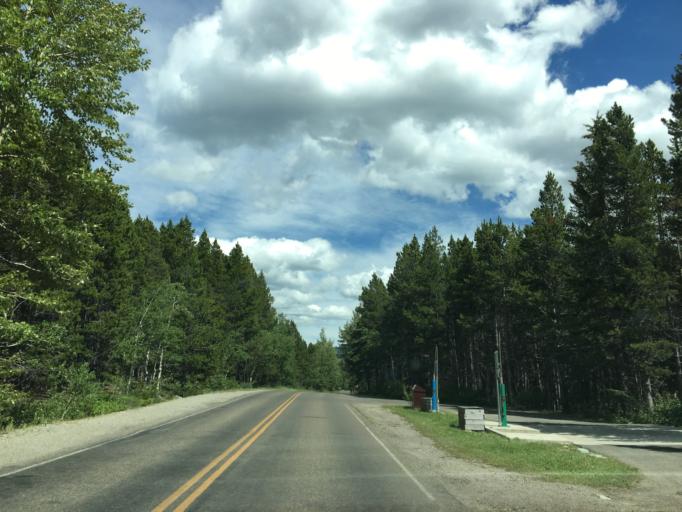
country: CA
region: Alberta
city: Cardston
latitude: 48.7977
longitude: -113.6730
